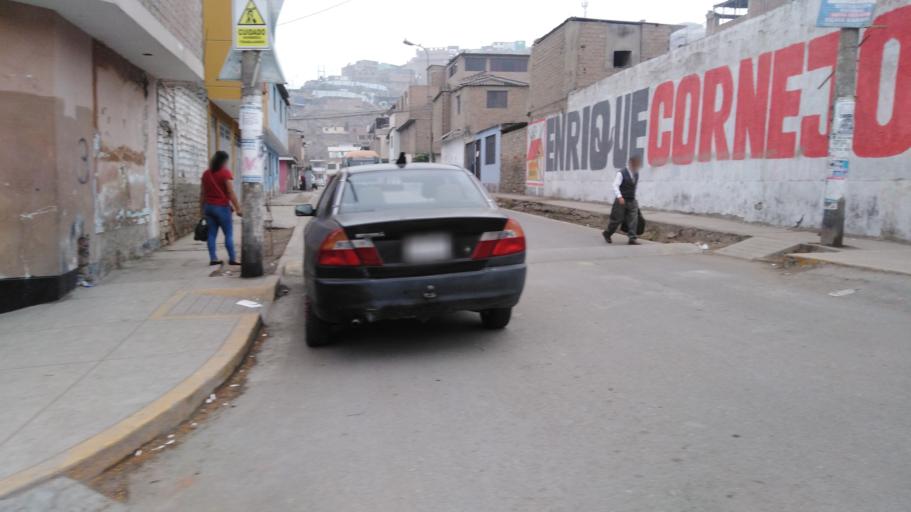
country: PE
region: Lima
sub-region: Lima
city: Surco
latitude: -12.1437
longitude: -76.9469
